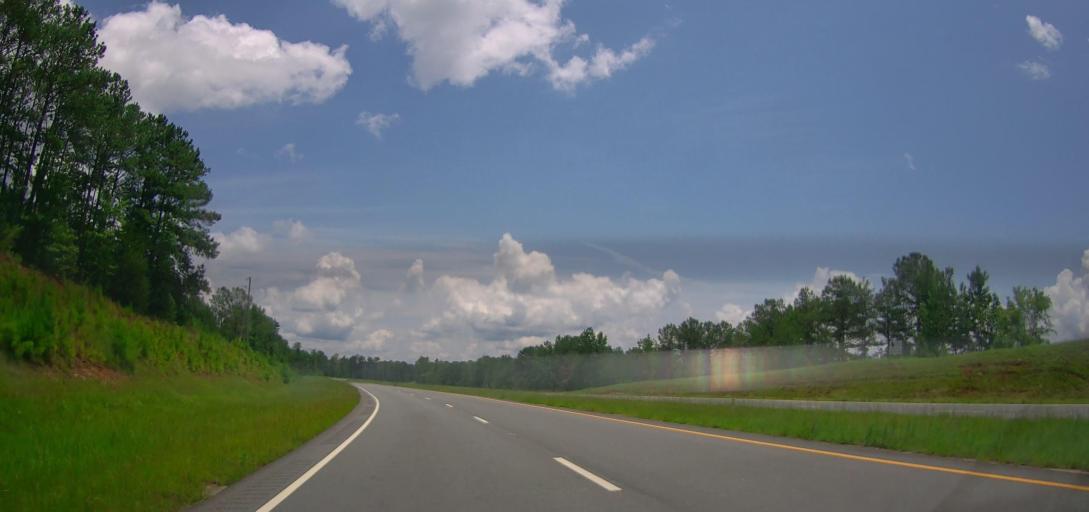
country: US
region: Georgia
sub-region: Upson County
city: Thomaston
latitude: 32.8182
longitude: -84.2950
